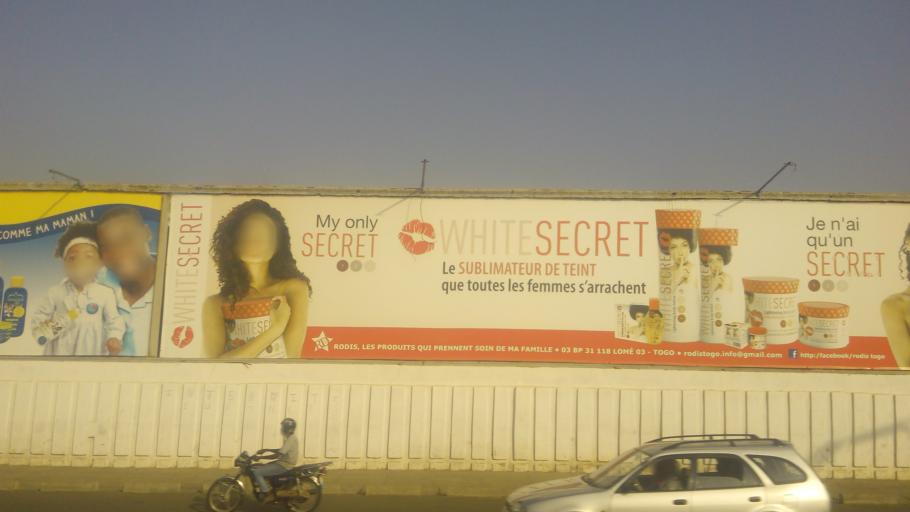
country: TG
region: Maritime
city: Lome
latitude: 6.1239
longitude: 1.2283
